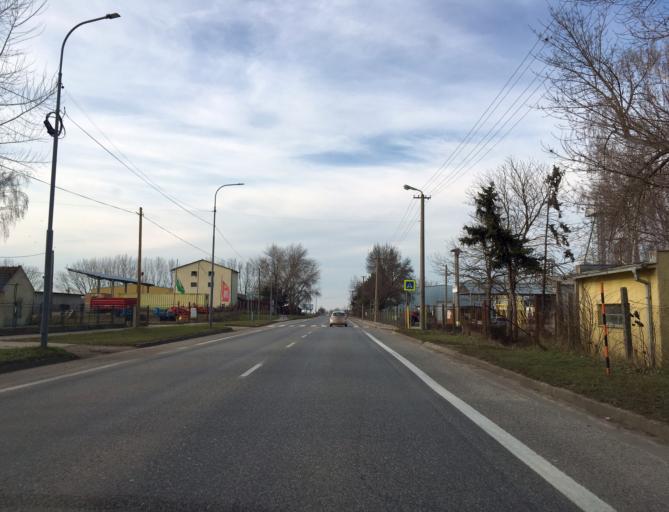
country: SK
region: Nitriansky
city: Surany
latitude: 48.1050
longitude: 18.0550
